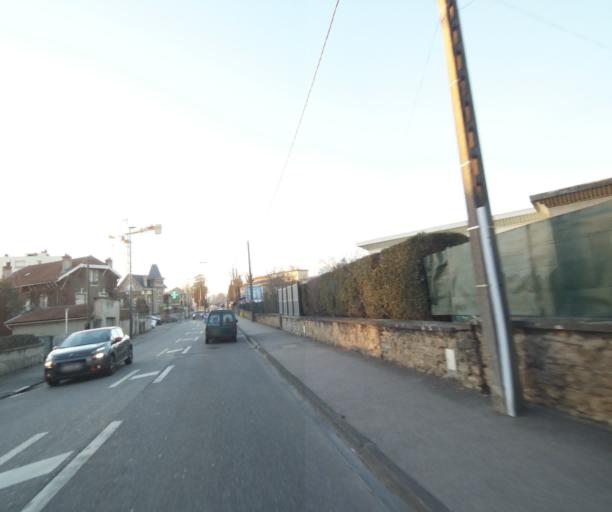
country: FR
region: Lorraine
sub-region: Departement de Meurthe-et-Moselle
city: Saint-Max
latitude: 48.7019
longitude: 6.1989
